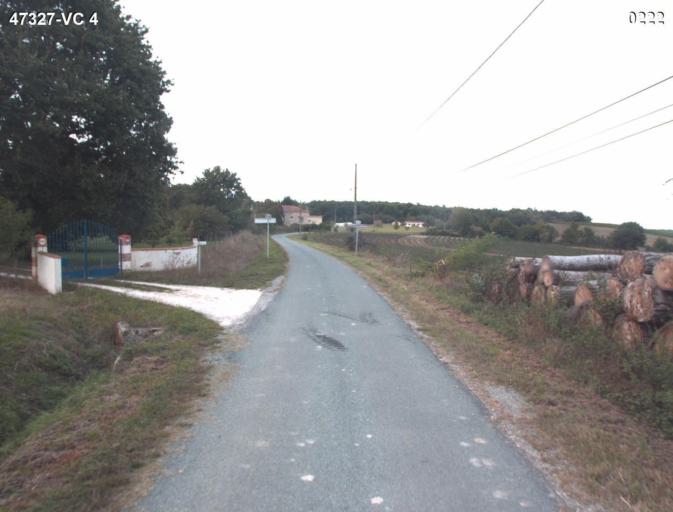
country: FR
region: Aquitaine
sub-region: Departement du Lot-et-Garonne
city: Barbaste
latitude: 44.2130
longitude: 0.2563
